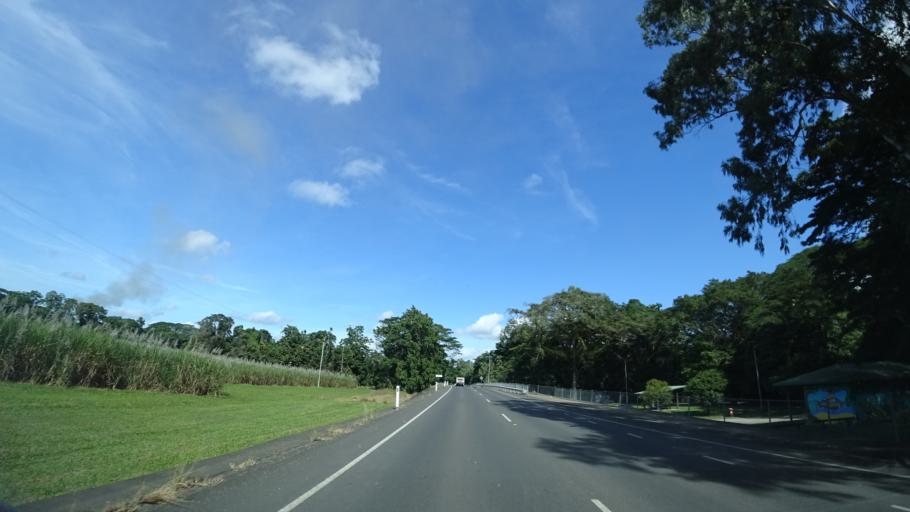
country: AU
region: Queensland
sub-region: Cairns
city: Port Douglas
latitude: -16.4516
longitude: 145.3716
